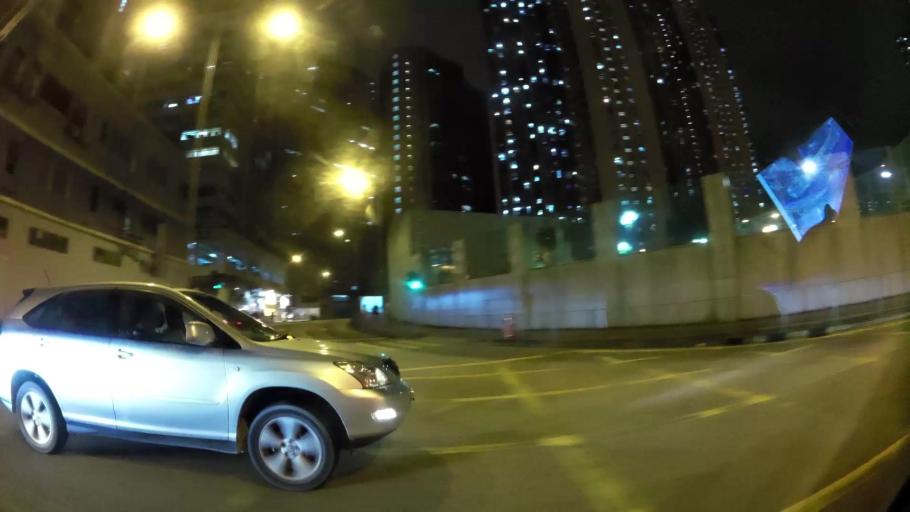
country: HK
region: Tsuen Wan
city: Tsuen Wan
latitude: 22.3692
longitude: 114.1296
